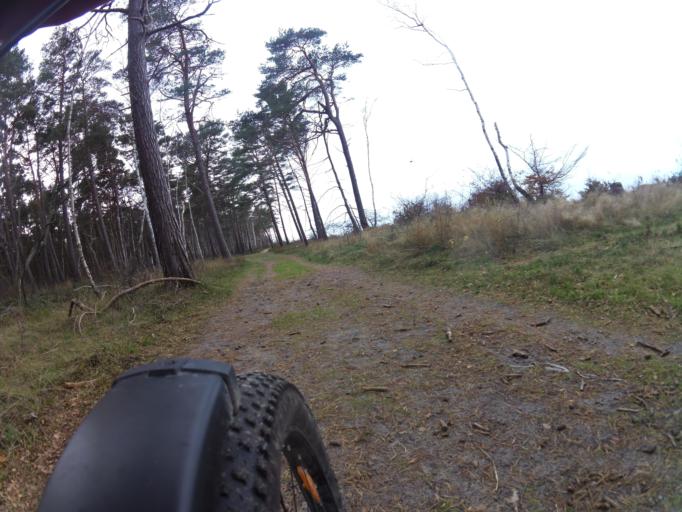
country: PL
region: Pomeranian Voivodeship
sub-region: Powiat wejherowski
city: Choczewo
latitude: 54.8100
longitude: 17.8277
